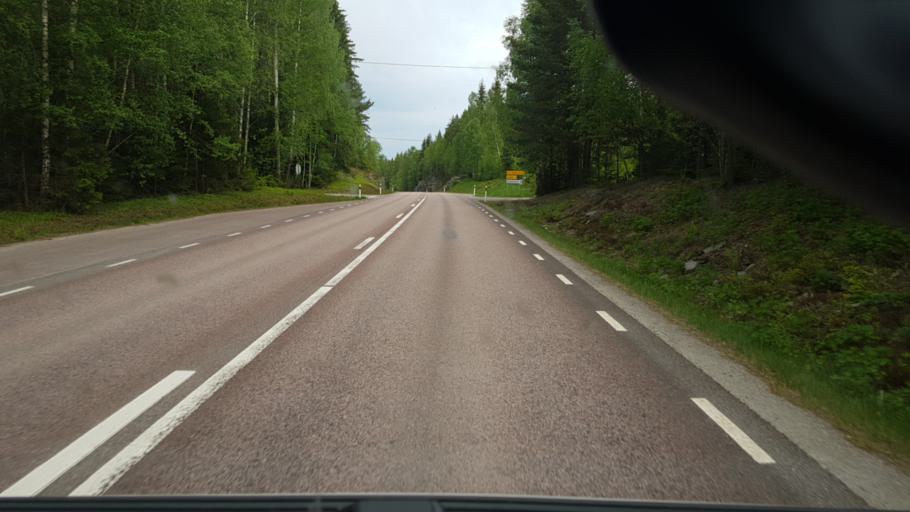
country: SE
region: Vaermland
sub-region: Arvika Kommun
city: Arvika
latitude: 59.5938
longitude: 12.6433
